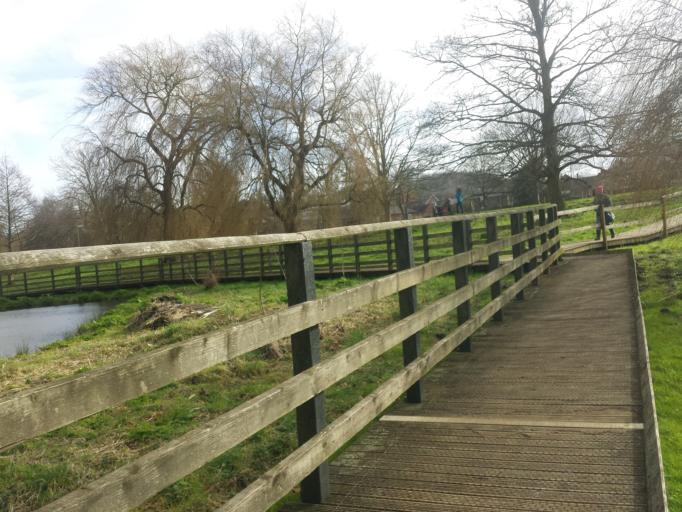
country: GB
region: England
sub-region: Surrey
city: Godalming
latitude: 51.1879
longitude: -0.6120
